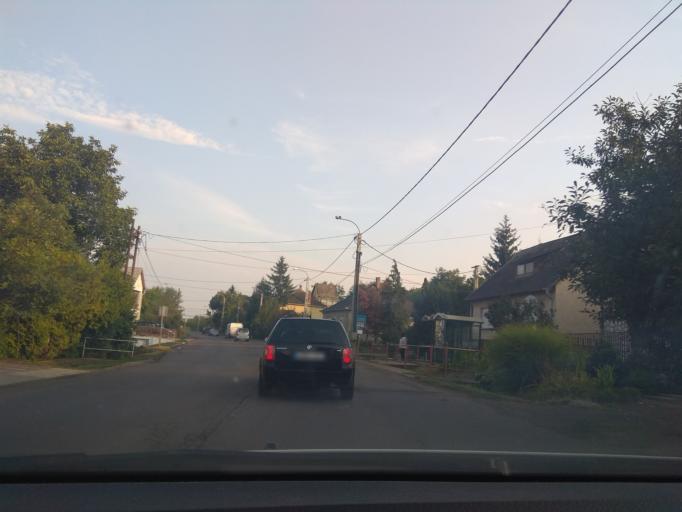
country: HU
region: Heves
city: Andornaktalya
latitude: 47.8646
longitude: 20.4071
